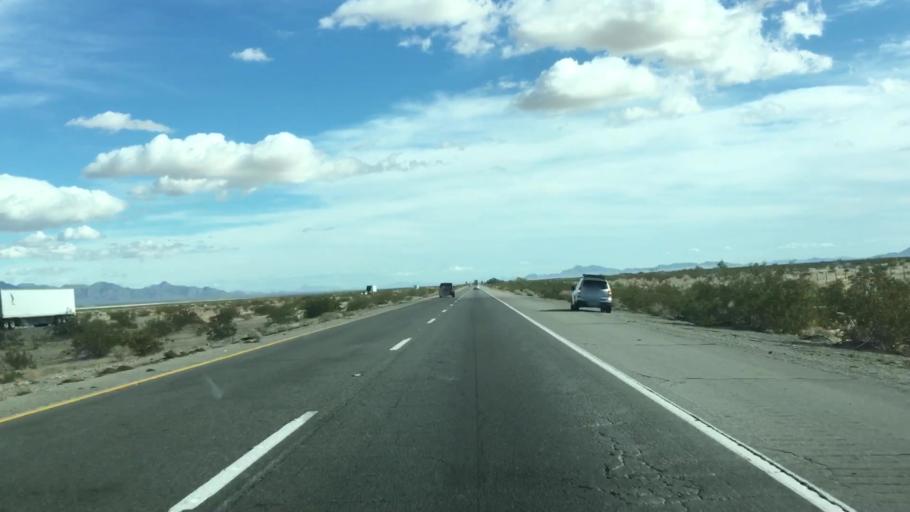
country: US
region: California
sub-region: Riverside County
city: Mesa Verde
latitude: 33.6431
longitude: -115.1096
